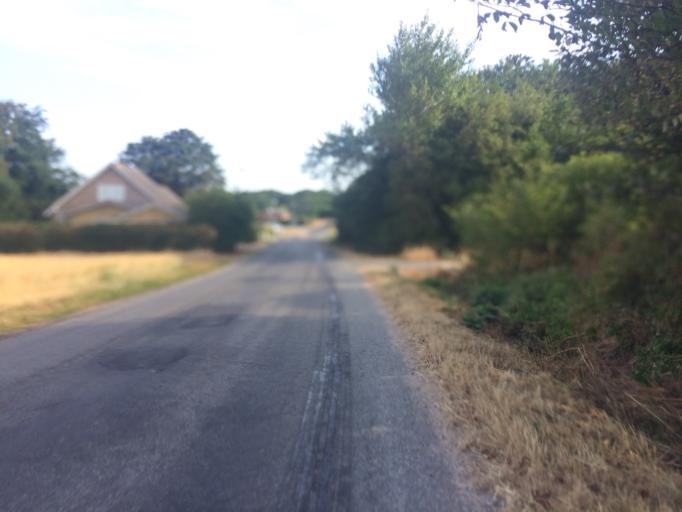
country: DK
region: Central Jutland
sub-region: Holstebro Kommune
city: Vinderup
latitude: 56.5992
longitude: 8.7596
